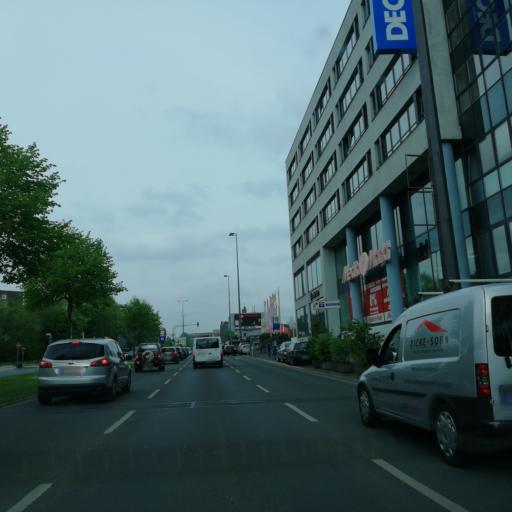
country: DE
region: North Rhine-Westphalia
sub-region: Regierungsbezirk Dusseldorf
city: Wuppertal
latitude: 51.2566
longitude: 7.1622
